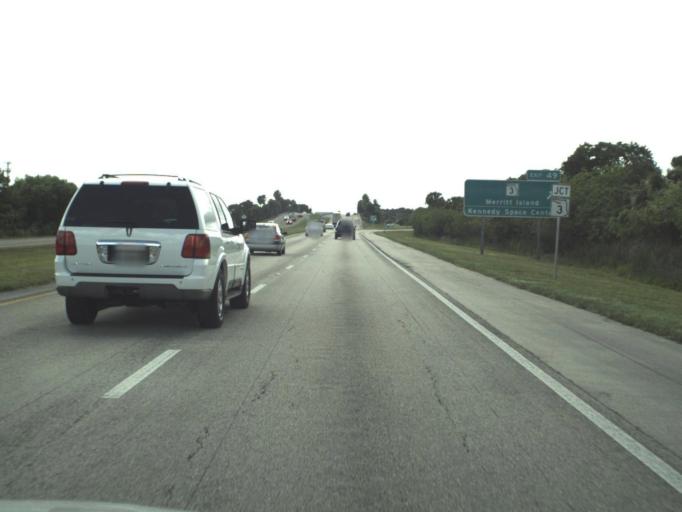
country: US
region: Florida
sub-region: Brevard County
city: Cocoa
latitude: 28.4054
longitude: -80.7004
